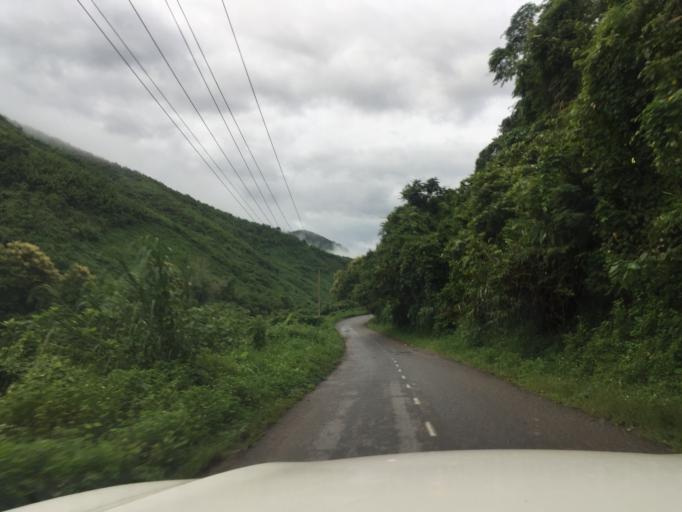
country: LA
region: Oudomxai
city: Muang La
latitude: 21.0415
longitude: 102.2415
